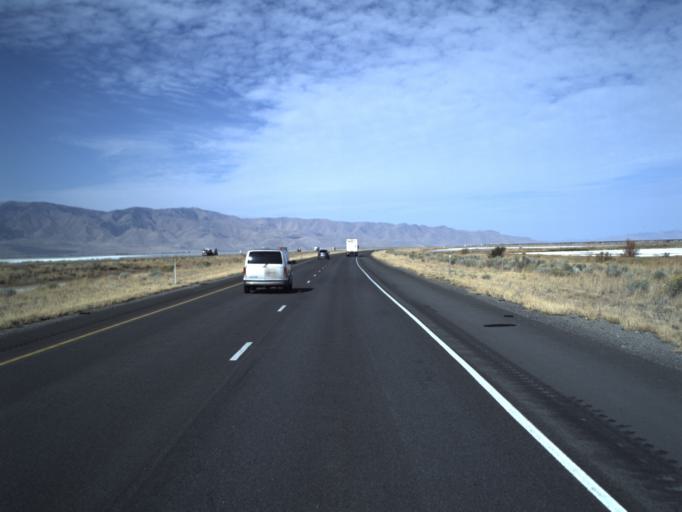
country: US
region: Utah
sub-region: Tooele County
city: Stansbury park
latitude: 40.6630
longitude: -112.3502
